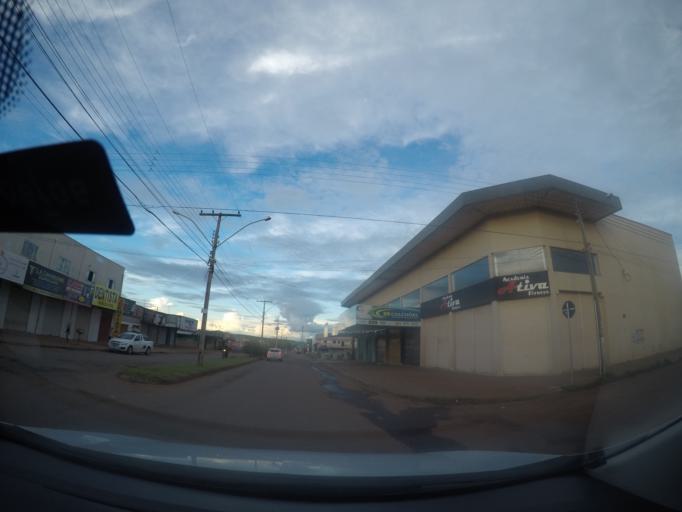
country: BR
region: Goias
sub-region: Goianira
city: Goianira
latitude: -16.5763
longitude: -49.3861
